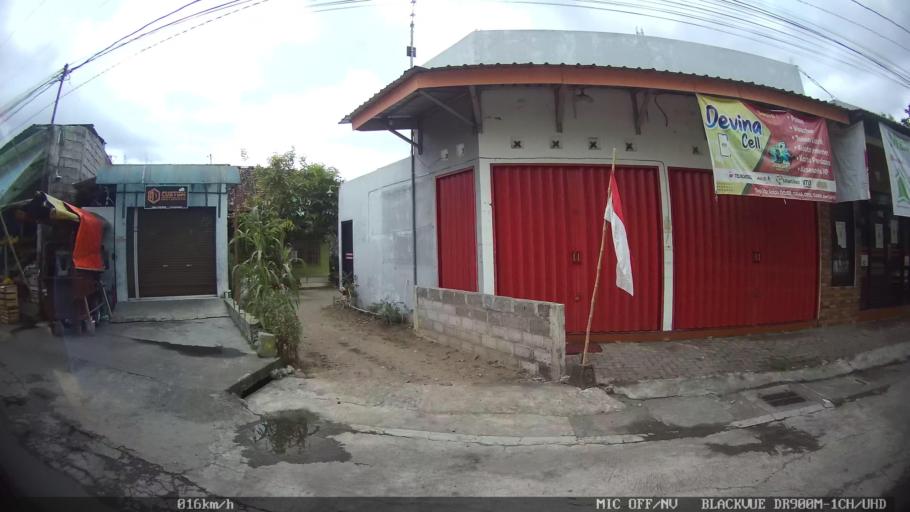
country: ID
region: Daerah Istimewa Yogyakarta
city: Depok
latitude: -7.8066
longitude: 110.4162
